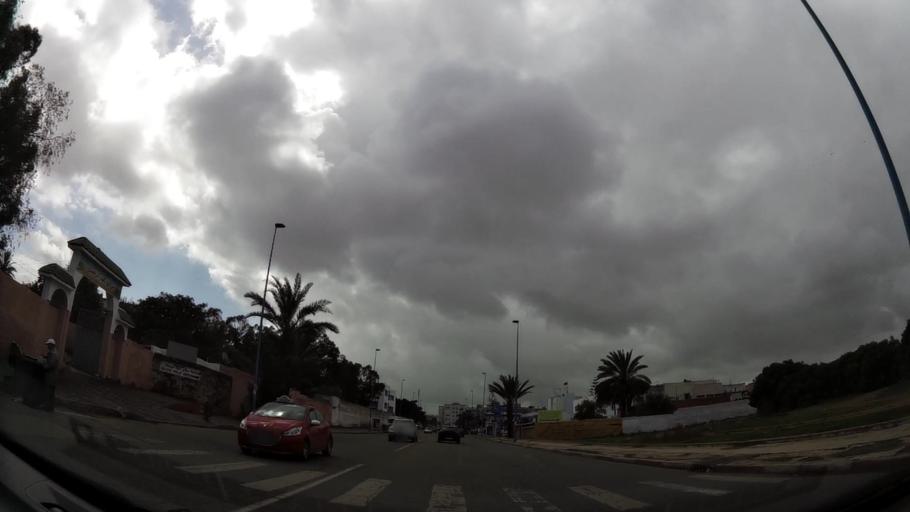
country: MA
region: Grand Casablanca
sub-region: Casablanca
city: Casablanca
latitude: 33.5427
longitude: -7.6016
